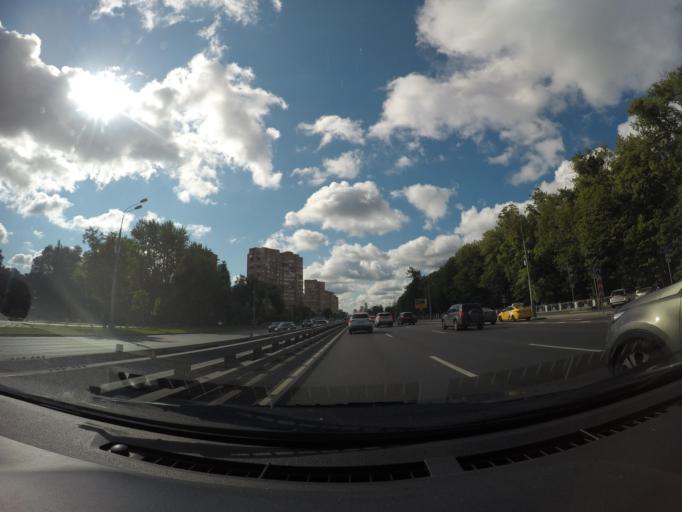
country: RU
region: Moskovskaya
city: Levoberezhnyy
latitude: 55.8513
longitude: 37.4730
